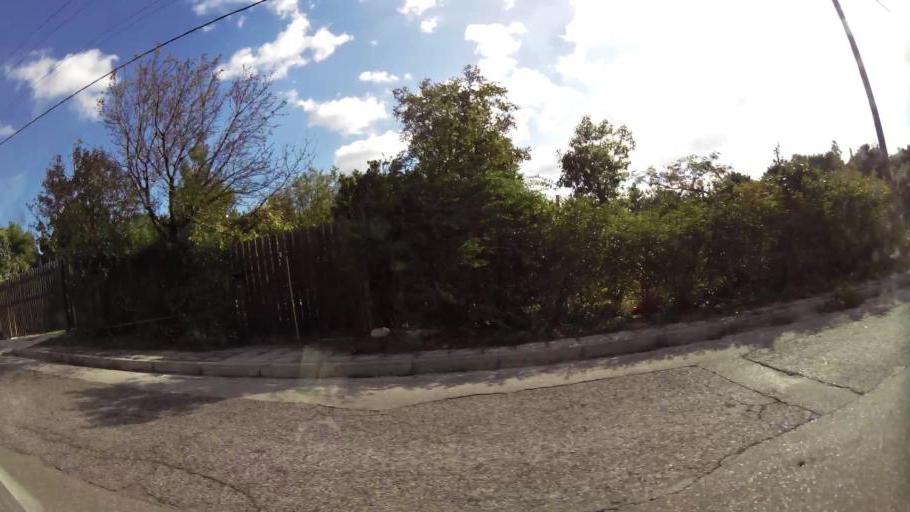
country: GR
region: Attica
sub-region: Nomarchia Anatolikis Attikis
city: Thrakomakedones
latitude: 38.1313
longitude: 23.7508
